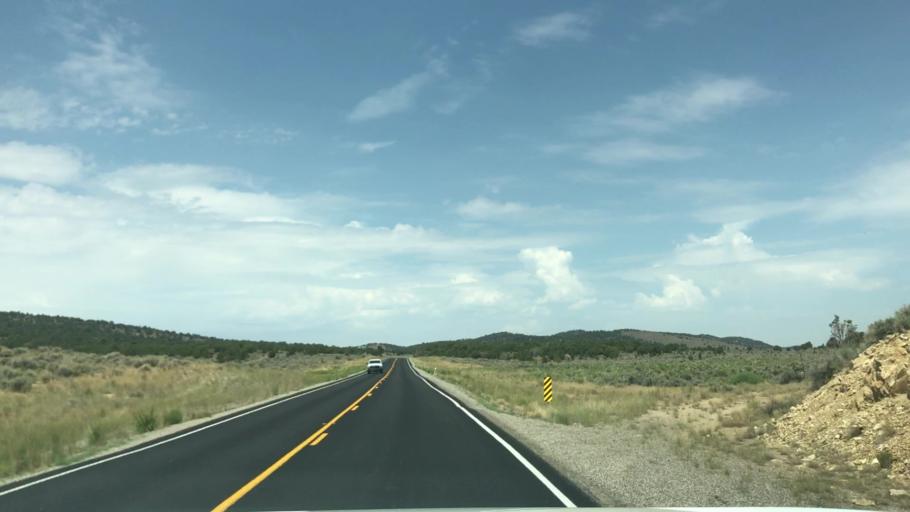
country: US
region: Nevada
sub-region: Eureka County
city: Eureka
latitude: 39.3894
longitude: -115.4500
